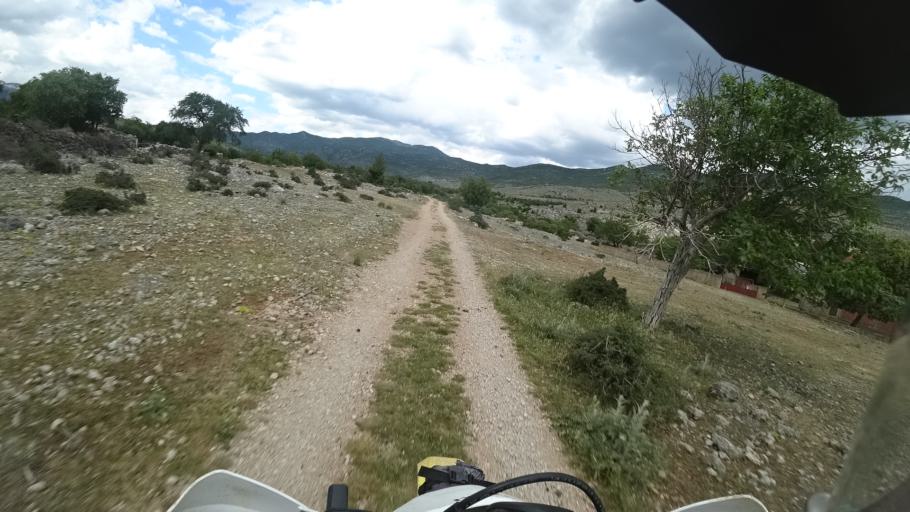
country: HR
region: Zadarska
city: Gracac
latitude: 44.1950
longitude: 15.9075
